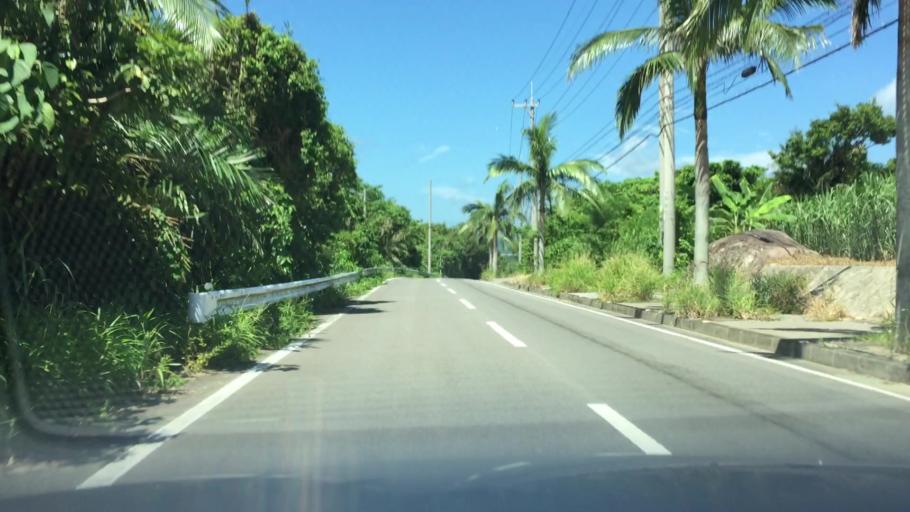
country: JP
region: Okinawa
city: Ishigaki
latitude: 24.4504
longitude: 124.1841
